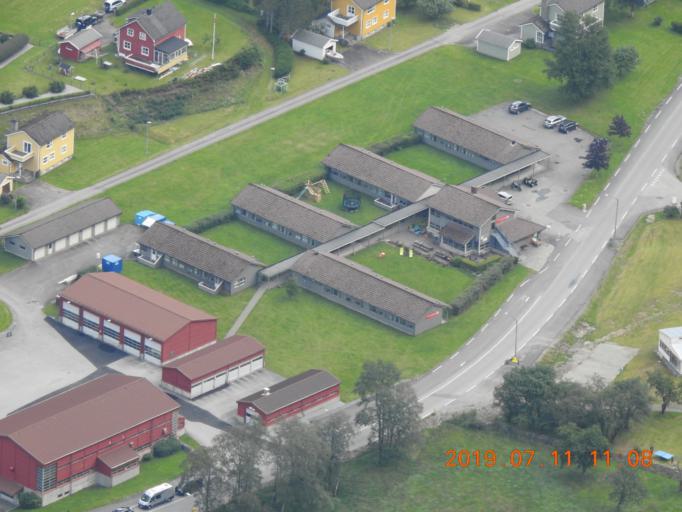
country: NO
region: Vest-Agder
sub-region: Sirdal
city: Tonstad
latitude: 59.0425
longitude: 6.6288
